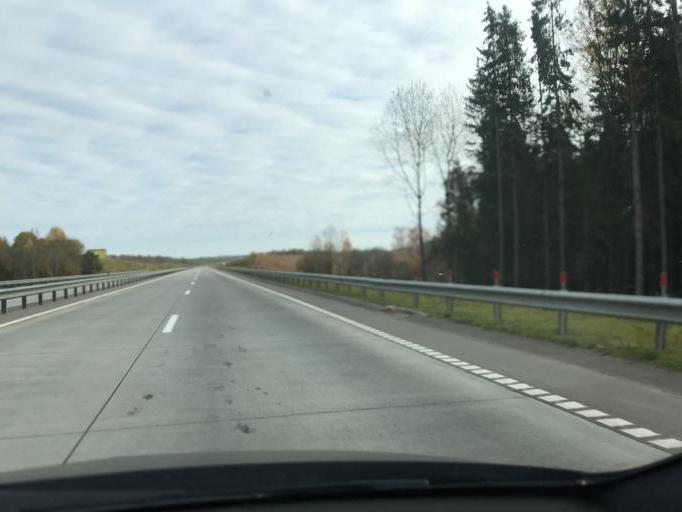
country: BY
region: Minsk
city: Syomkava
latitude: 54.0639
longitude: 27.4279
